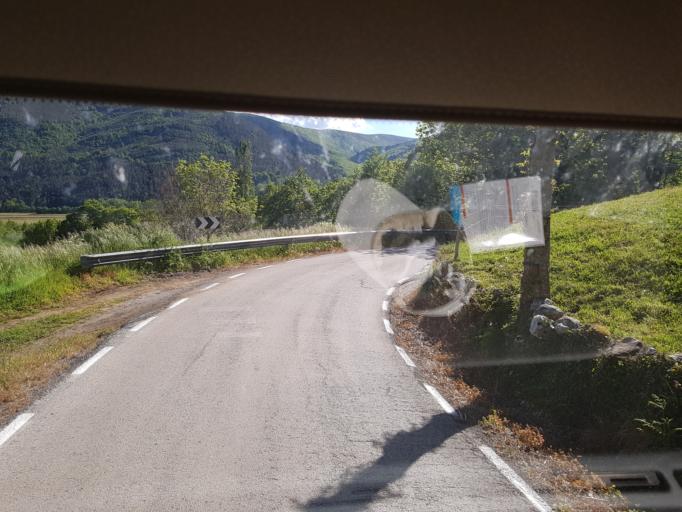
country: ES
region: Castille and Leon
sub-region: Provincia de Burgos
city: Espinosa de los Monteros
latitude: 43.1233
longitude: -3.5792
